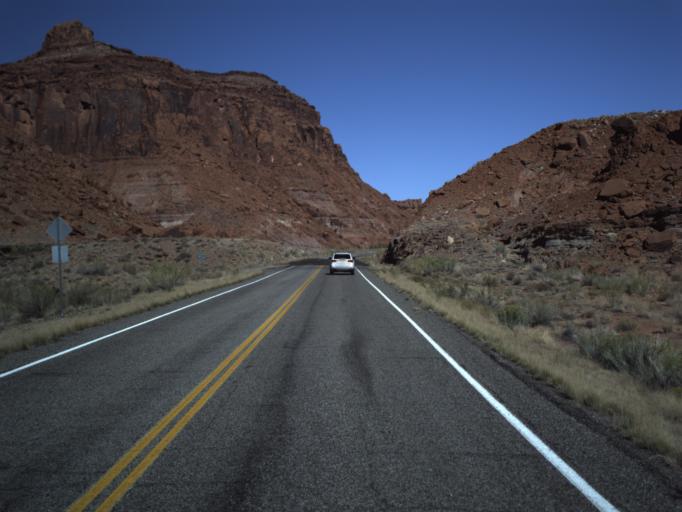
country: US
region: Utah
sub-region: San Juan County
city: Blanding
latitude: 37.9319
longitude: -110.4659
